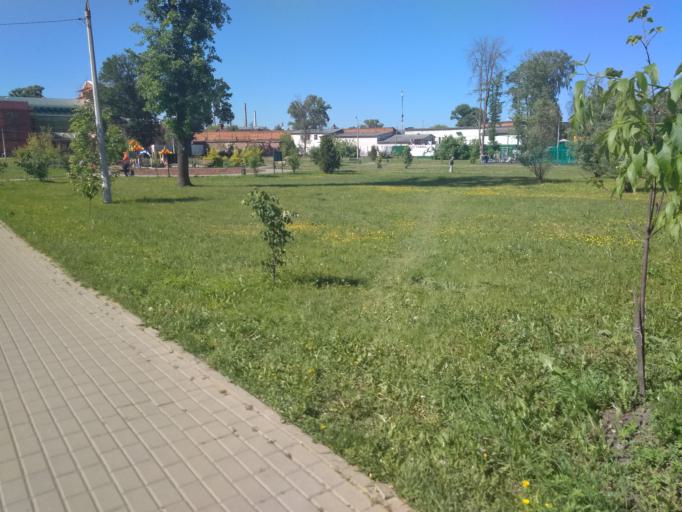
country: RU
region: Moskovskaya
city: Orekhovo-Zuyevo
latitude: 55.8016
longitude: 38.9970
